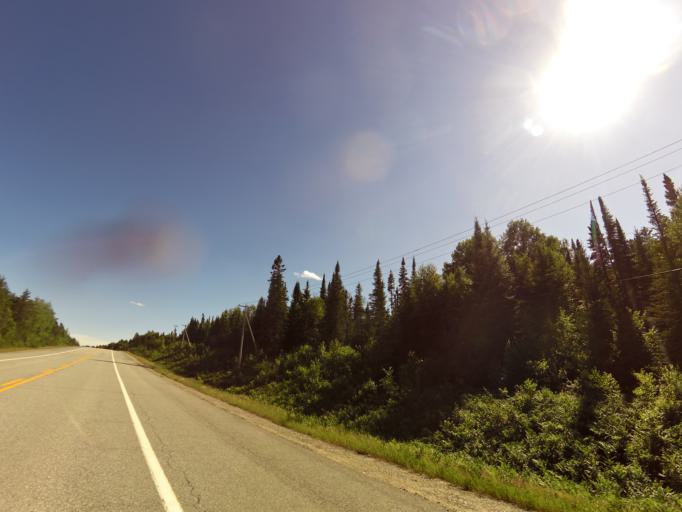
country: CA
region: Quebec
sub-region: Abitibi-Temiscamingue
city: Val-d'Or
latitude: 47.9378
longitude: -77.3610
